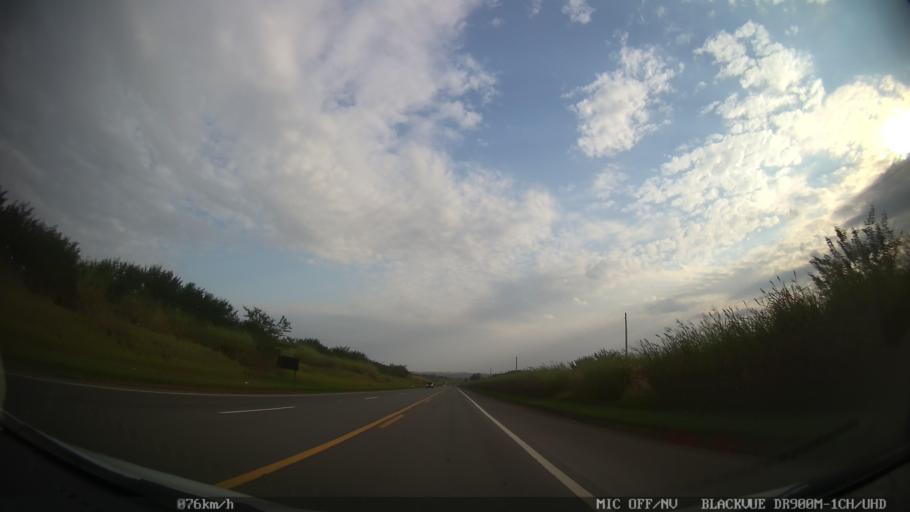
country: BR
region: Sao Paulo
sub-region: Cosmopolis
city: Cosmopolis
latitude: -22.6205
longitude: -47.2516
